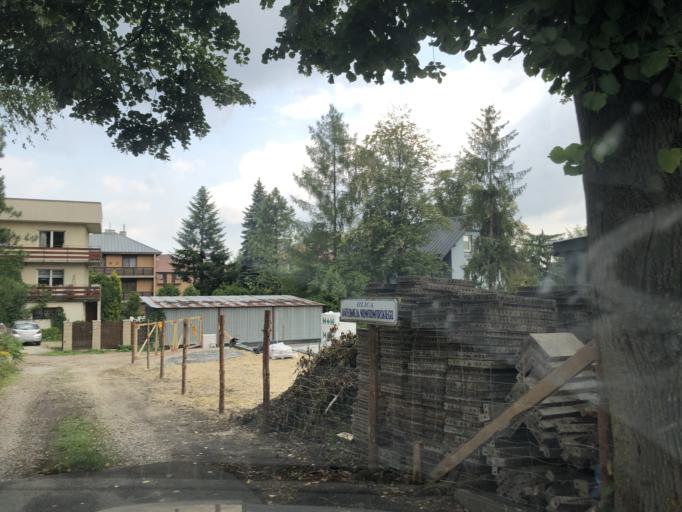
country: PL
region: Lesser Poland Voivodeship
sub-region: Powiat krakowski
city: Libertow
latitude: 50.0023
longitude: 19.9268
